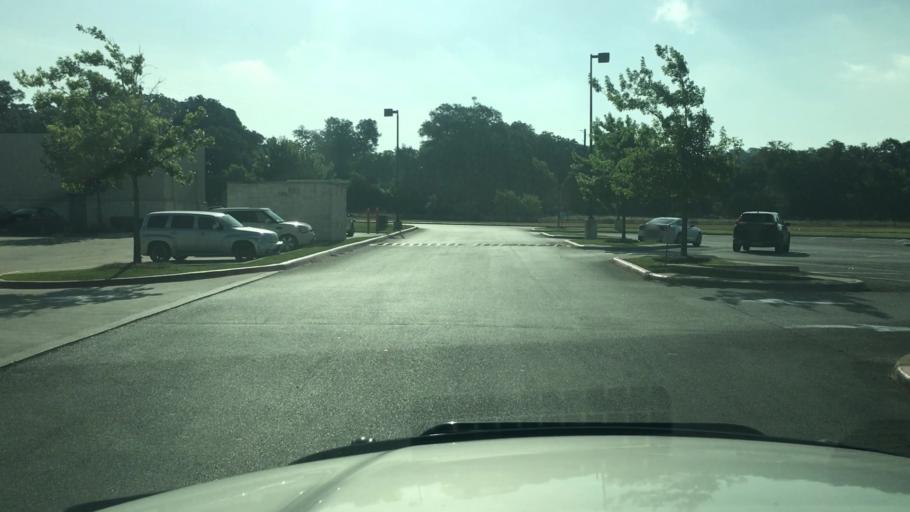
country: US
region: Texas
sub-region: Hays County
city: Dripping Springs
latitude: 30.1907
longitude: -98.0813
